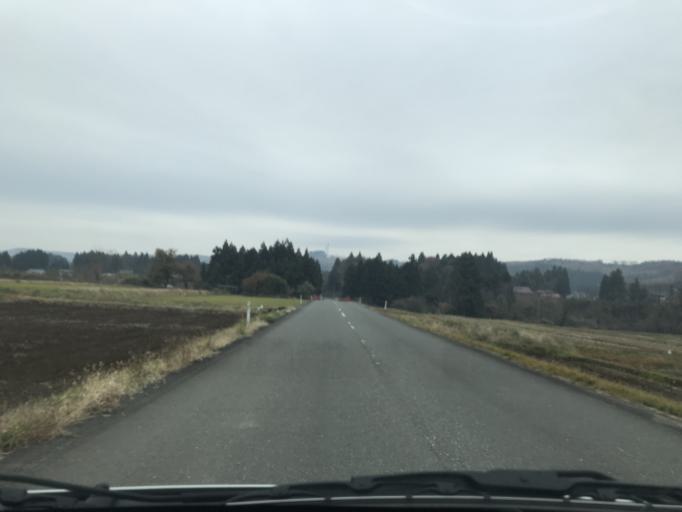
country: JP
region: Iwate
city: Mizusawa
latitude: 39.0261
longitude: 141.0731
